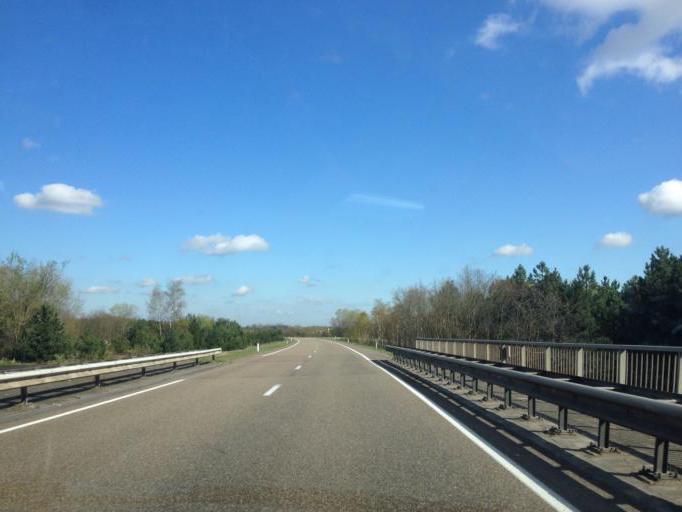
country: BE
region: Flanders
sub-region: Provincie Limburg
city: Overpelt
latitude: 51.2390
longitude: 5.4094
